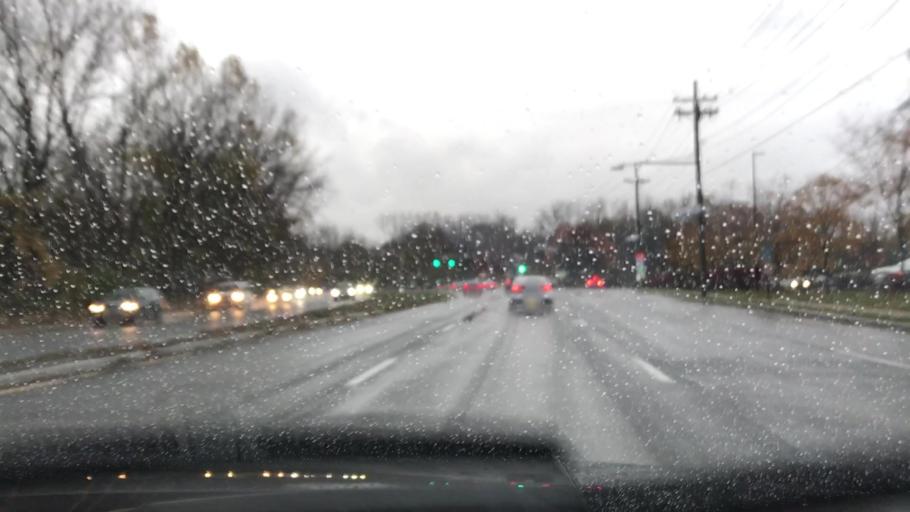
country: US
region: New Jersey
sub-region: Bergen County
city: Leonia
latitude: 40.8708
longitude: -74.0054
